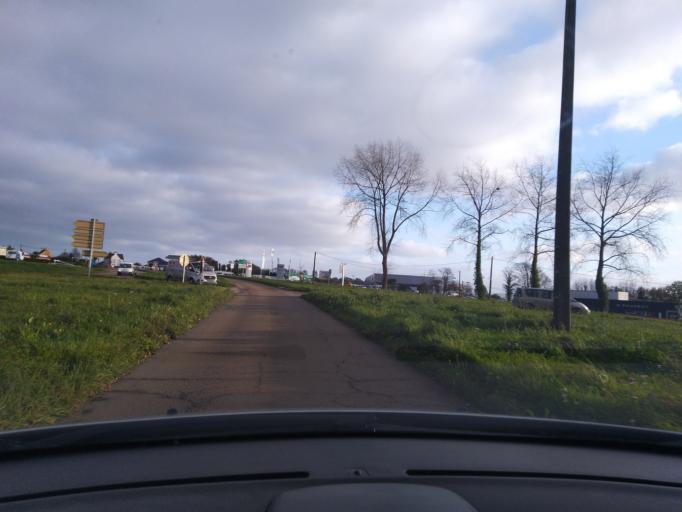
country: FR
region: Brittany
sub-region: Departement du Finistere
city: Morlaix
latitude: 48.5794
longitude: -3.7979
